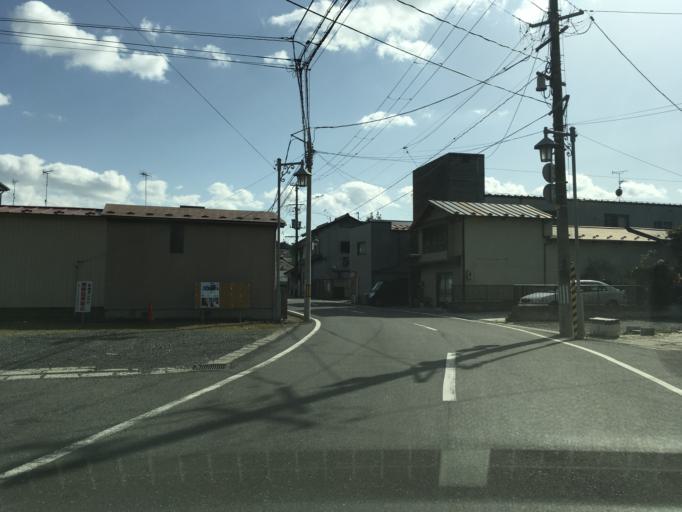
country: JP
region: Miyagi
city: Wakuya
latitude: 38.6550
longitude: 141.2841
